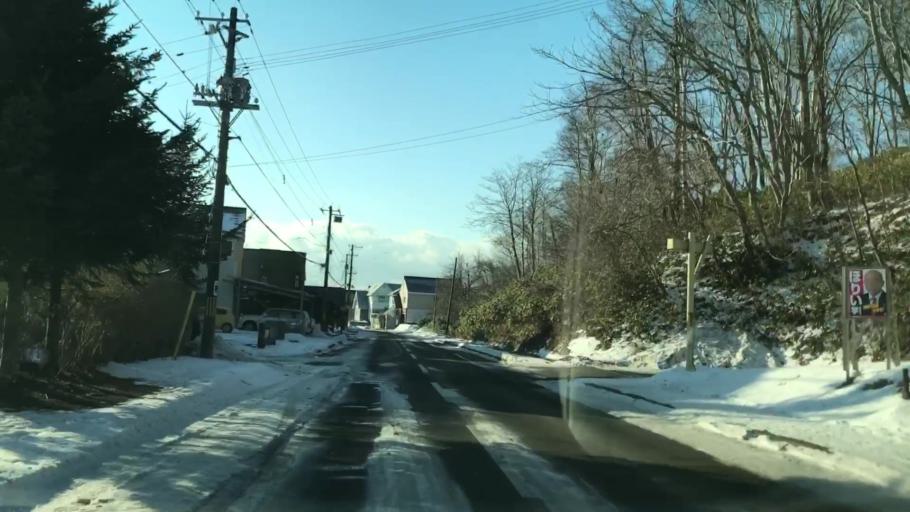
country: JP
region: Hokkaido
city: Muroran
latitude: 42.3882
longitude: 141.0653
